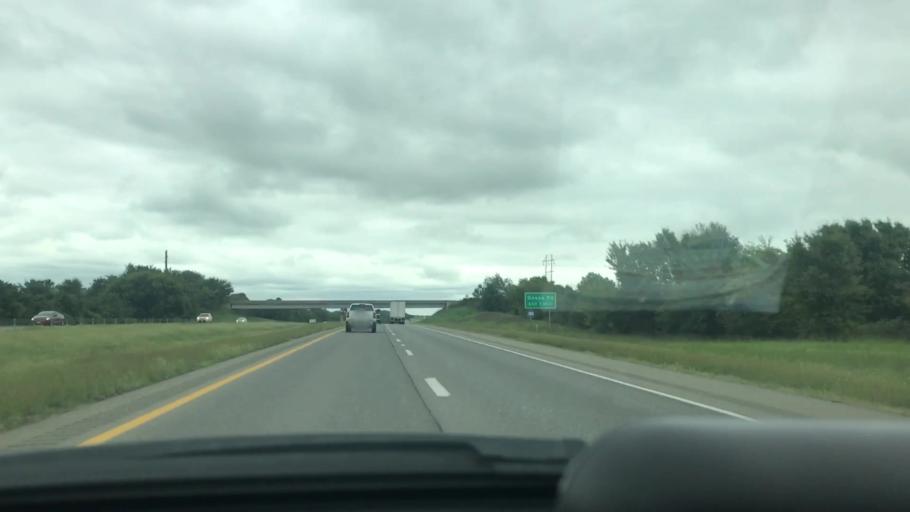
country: US
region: Oklahoma
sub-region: McIntosh County
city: Checotah
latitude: 35.3889
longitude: -95.5662
